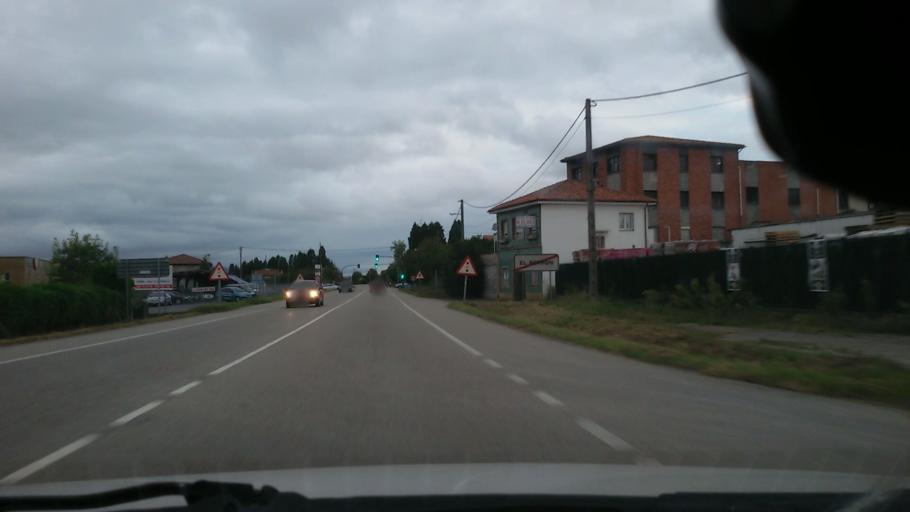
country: ES
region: Asturias
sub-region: Province of Asturias
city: Norena
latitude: 43.3849
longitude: -5.7080
